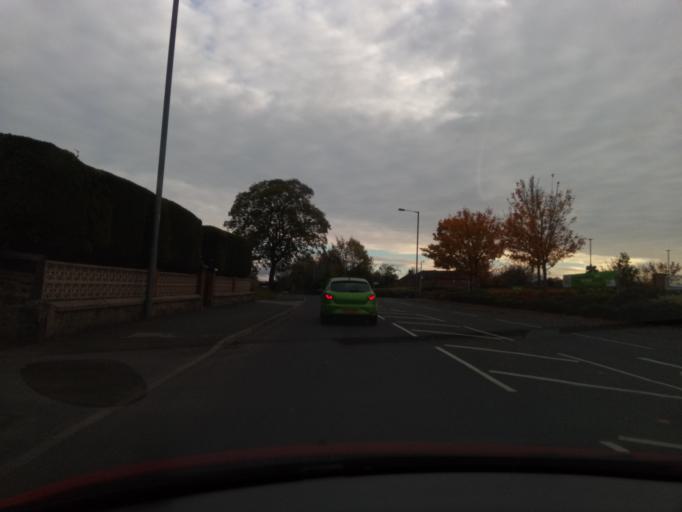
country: GB
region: England
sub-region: County Durham
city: Bishop Auckland
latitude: 54.6582
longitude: -1.6717
